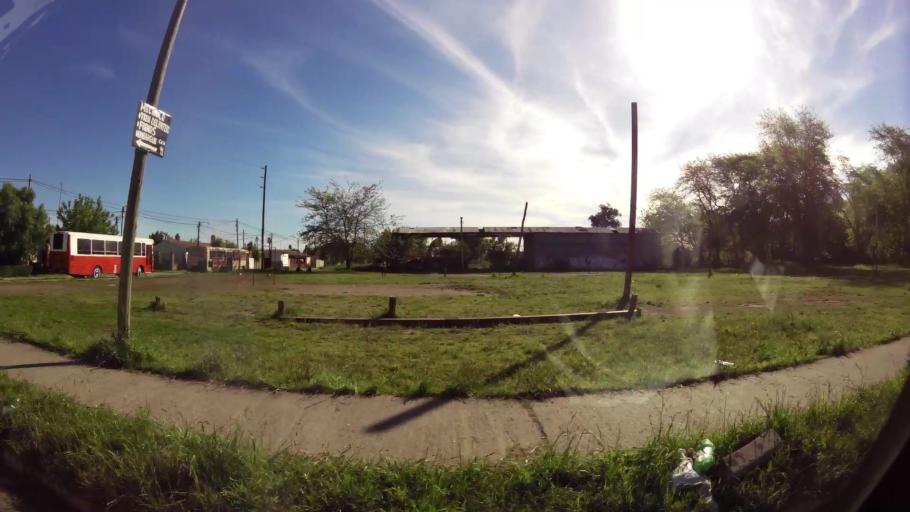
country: AR
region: Buenos Aires
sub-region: Partido de Almirante Brown
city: Adrogue
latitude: -34.8287
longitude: -58.3525
